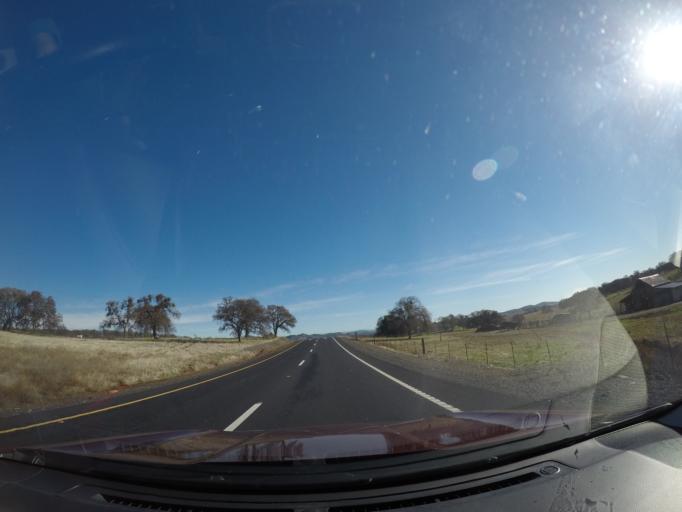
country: US
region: California
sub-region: Calaveras County
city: Copperopolis
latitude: 37.8463
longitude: -120.5613
